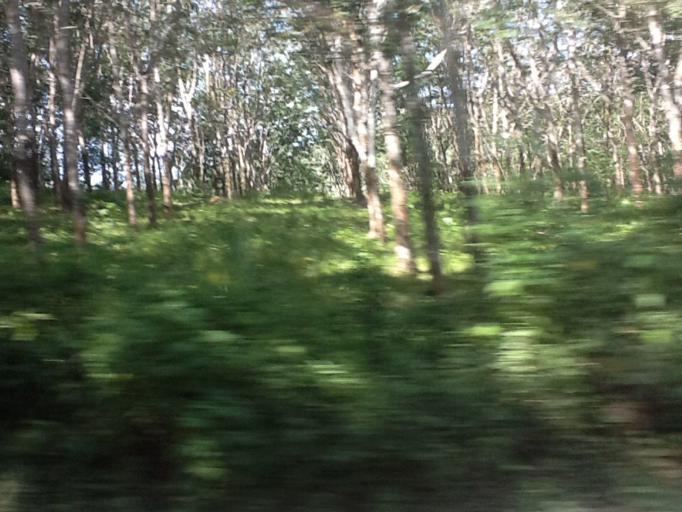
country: TH
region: Phuket
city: Thalang
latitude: 8.1212
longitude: 98.3283
